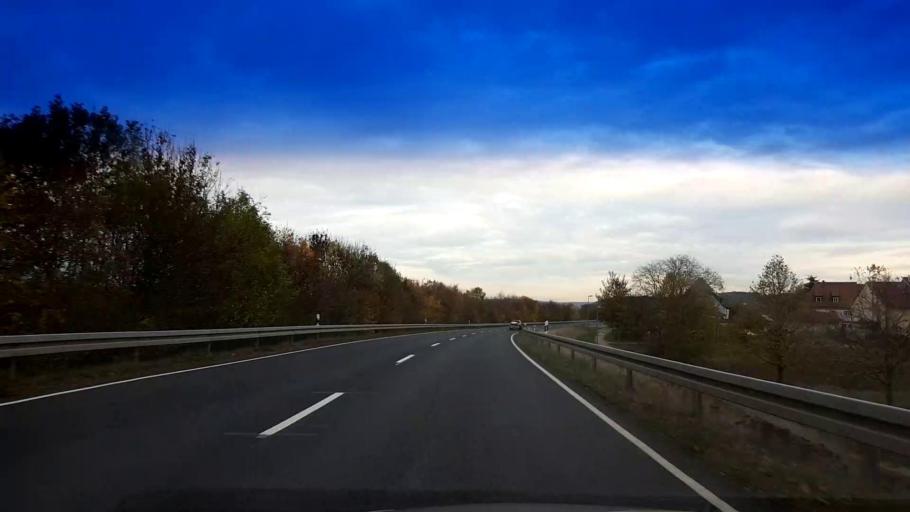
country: DE
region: Bavaria
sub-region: Upper Franconia
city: Viereth-Trunstadt
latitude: 49.9311
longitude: 10.7491
